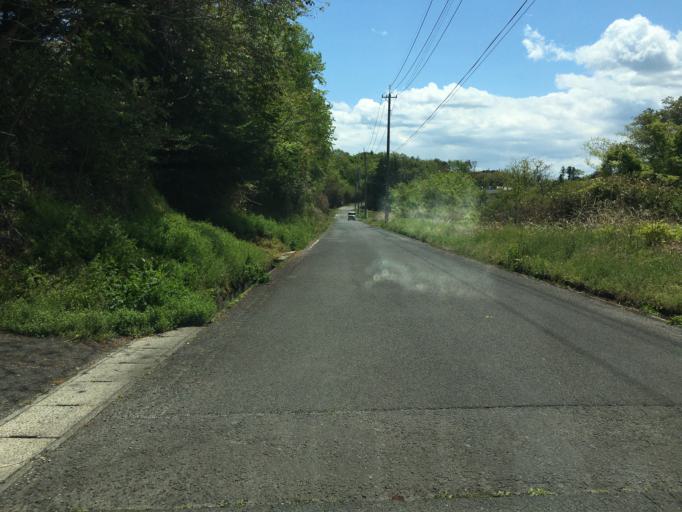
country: JP
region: Miyagi
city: Marumori
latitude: 37.8125
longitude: 140.9481
